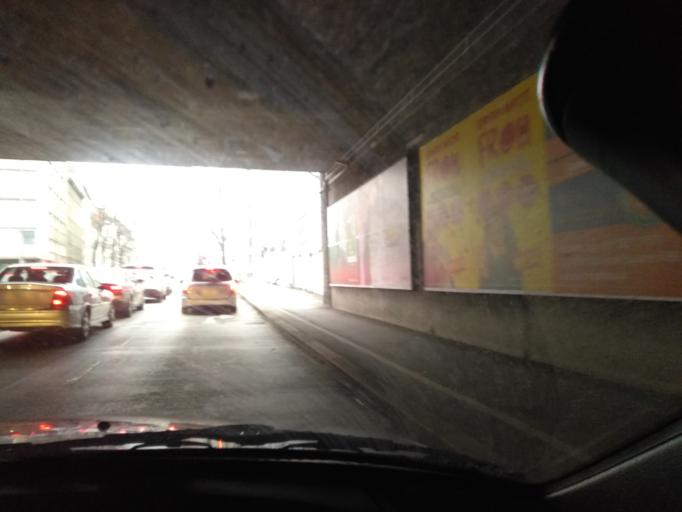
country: AT
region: Vienna
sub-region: Wien Stadt
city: Vienna
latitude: 48.1762
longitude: 16.3417
